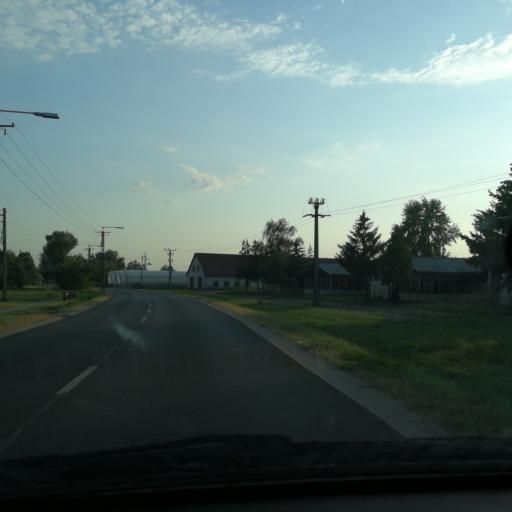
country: HU
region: Bacs-Kiskun
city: Kiskunmajsa
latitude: 46.4925
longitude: 19.7231
